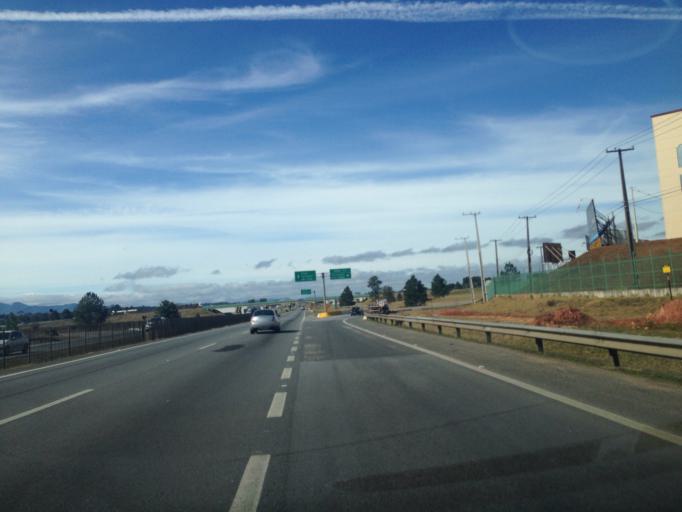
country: BR
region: Parana
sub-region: Sao Jose Dos Pinhais
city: Sao Jose dos Pinhais
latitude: -25.5098
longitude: -49.1322
